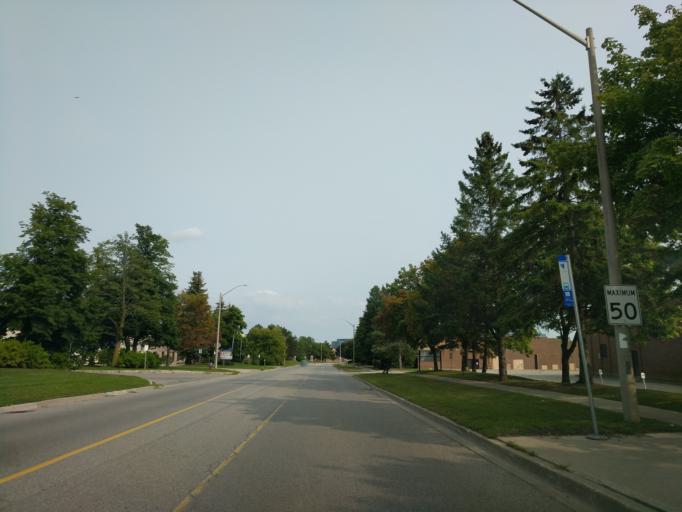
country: CA
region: Ontario
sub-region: York
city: Richmond Hill
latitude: 43.8498
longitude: -79.3904
